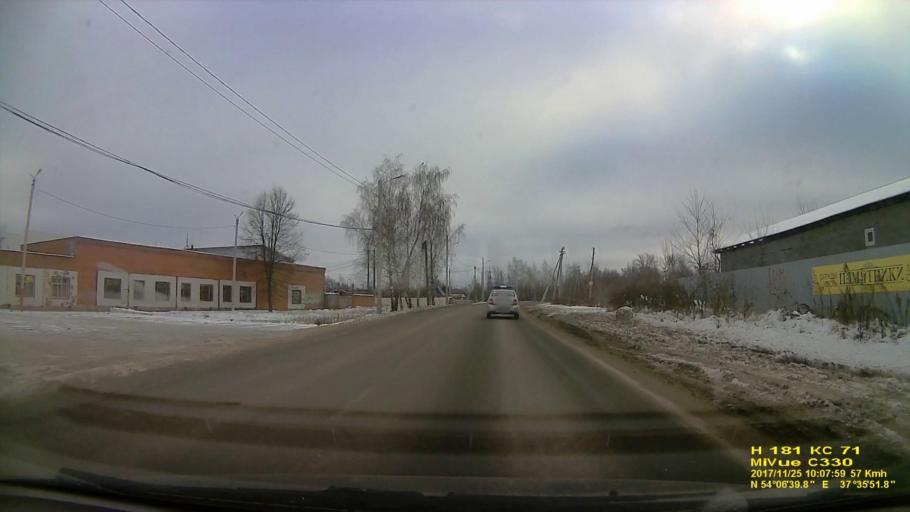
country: RU
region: Tula
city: Skuratovskiy
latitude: 54.1109
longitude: 37.5980
